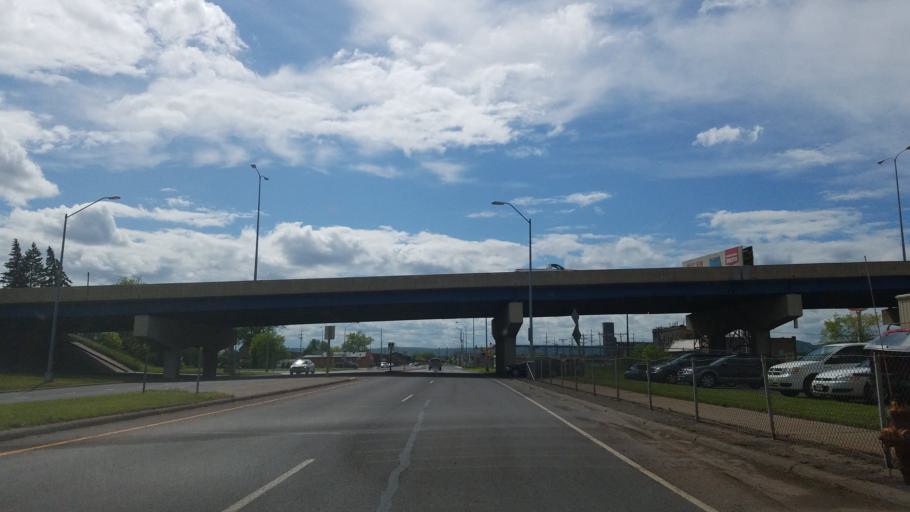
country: US
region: Wisconsin
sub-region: Douglas County
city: Superior
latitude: 46.7352
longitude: -92.0965
